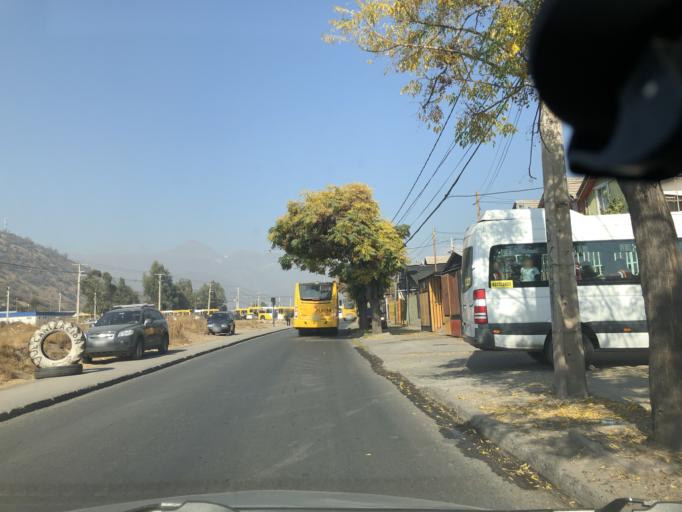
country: CL
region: Santiago Metropolitan
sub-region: Provincia de Cordillera
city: Puente Alto
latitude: -33.6024
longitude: -70.5557
